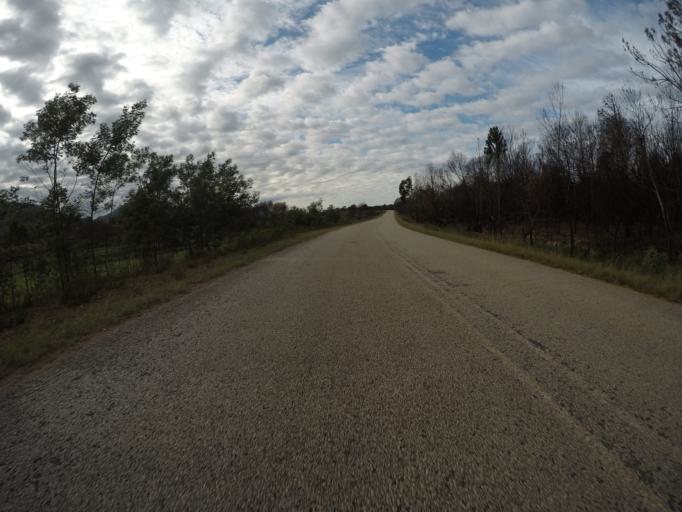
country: ZA
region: Eastern Cape
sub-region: Cacadu District Municipality
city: Kareedouw
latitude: -34.0119
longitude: 24.3127
